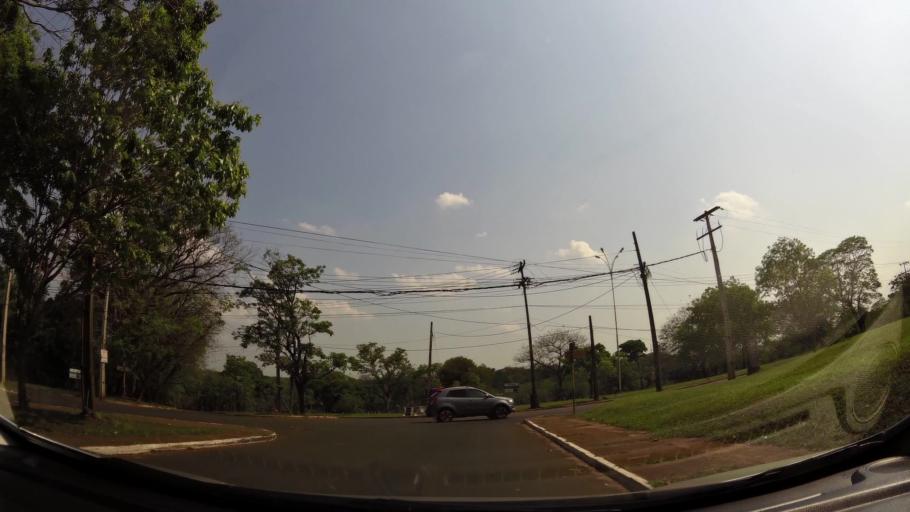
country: PY
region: Alto Parana
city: Ciudad del Este
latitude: -25.5127
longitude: -54.6308
